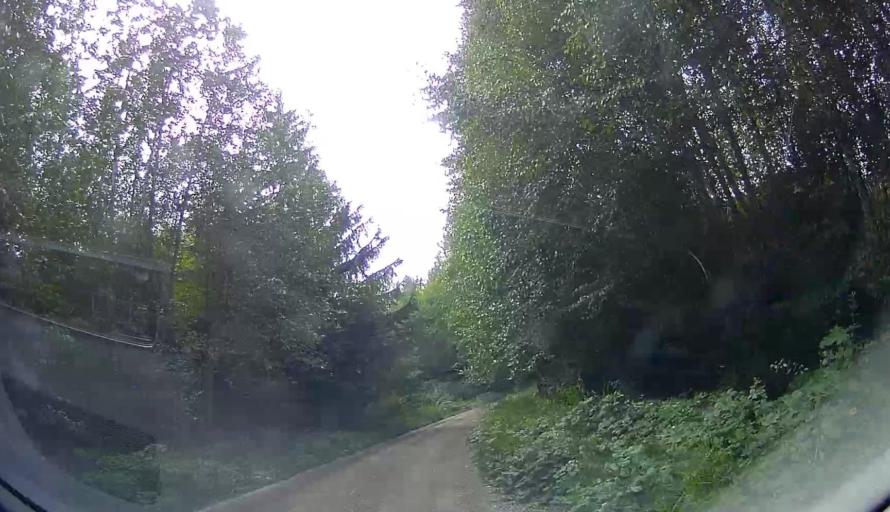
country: US
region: Washington
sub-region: Whatcom County
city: Sudden Valley
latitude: 48.6194
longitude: -122.3719
